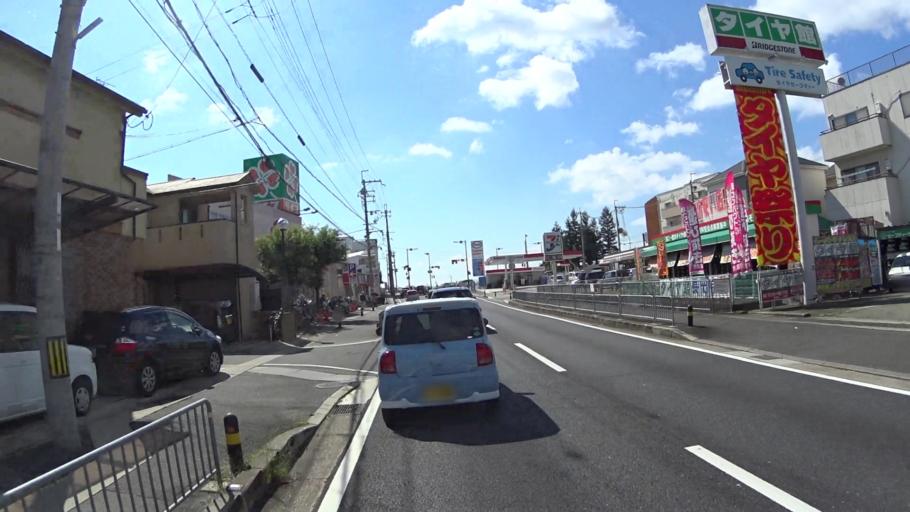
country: JP
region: Kyoto
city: Muko
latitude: 34.9364
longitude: 135.7033
